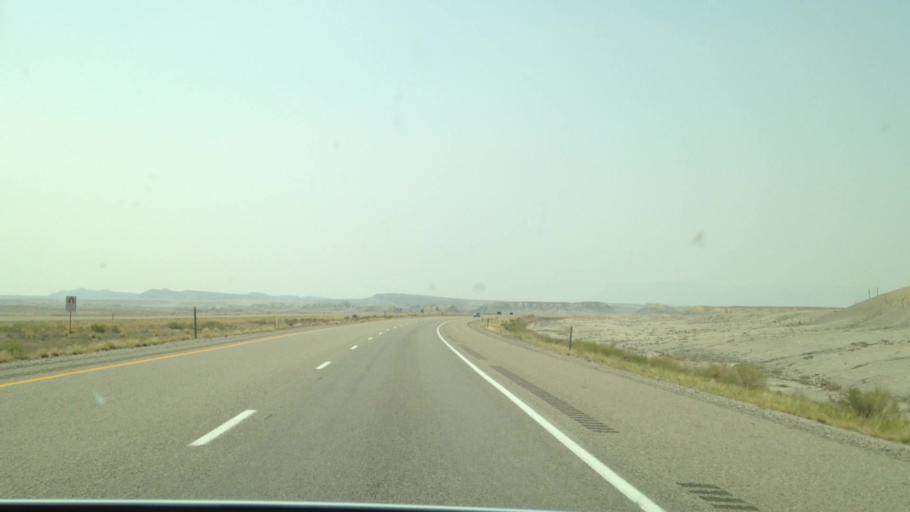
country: US
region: Utah
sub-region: Grand County
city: Moab
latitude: 38.9287
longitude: -110.0071
